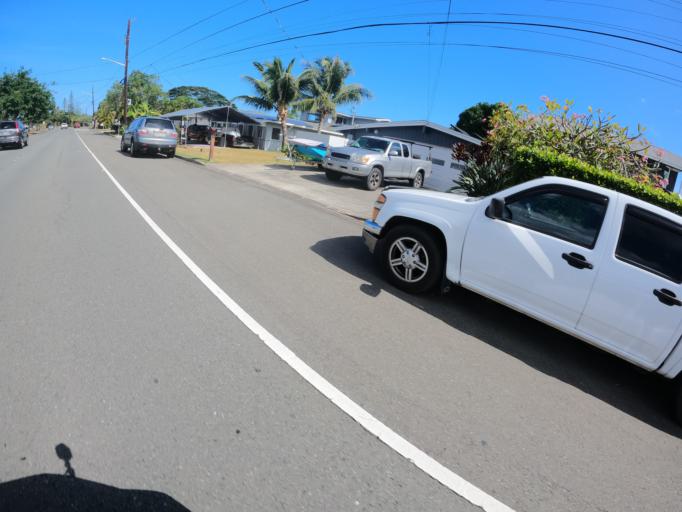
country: US
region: Hawaii
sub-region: Honolulu County
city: Kailua
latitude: 21.4127
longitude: -157.7525
